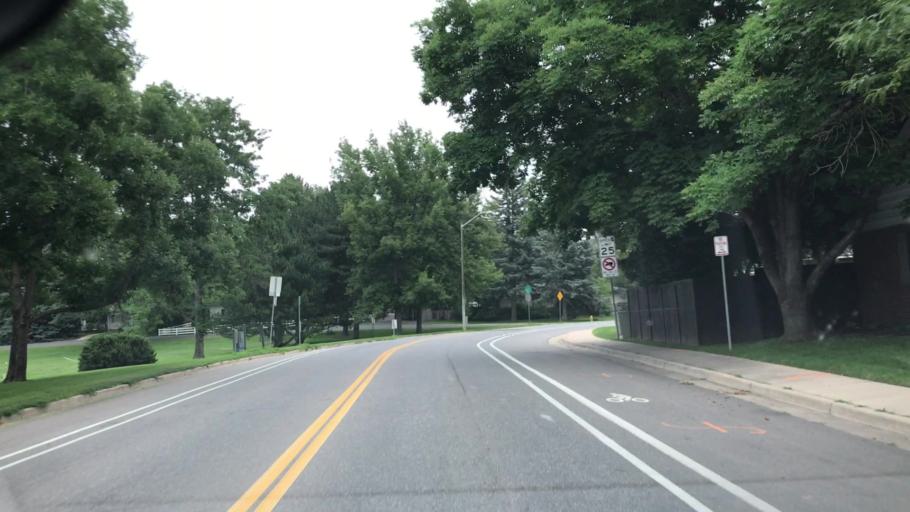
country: US
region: Colorado
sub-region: Arapahoe County
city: Cherry Hills Village
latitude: 39.6676
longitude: -104.9513
